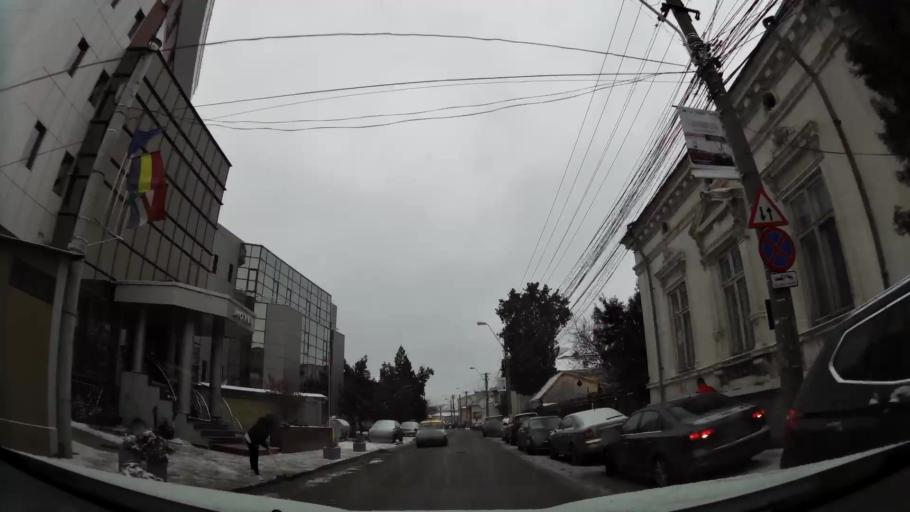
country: RO
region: Prahova
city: Ploiesti
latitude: 44.9343
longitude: 26.0260
